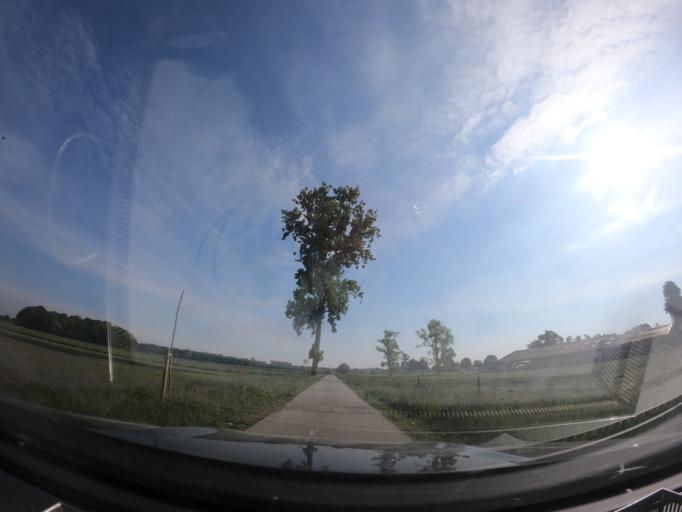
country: BE
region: Flanders
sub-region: Provincie Antwerpen
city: Olen
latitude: 51.1255
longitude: 4.8146
